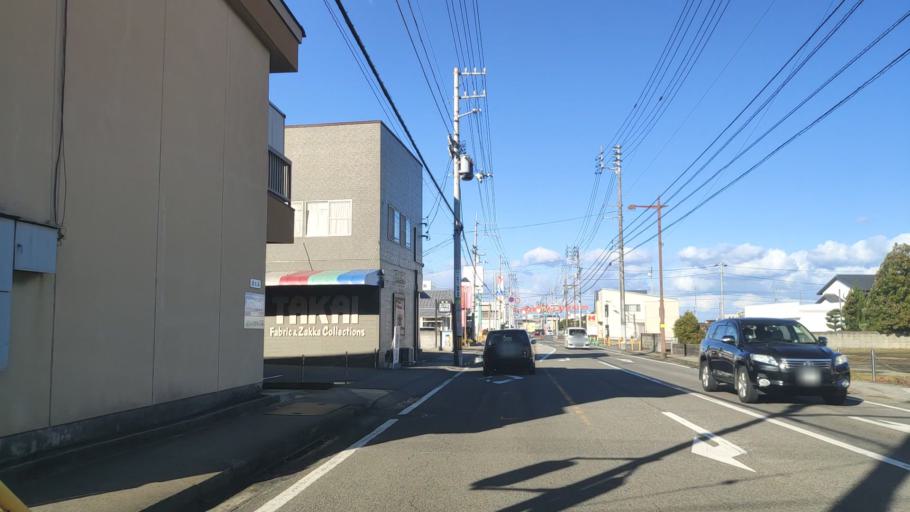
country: JP
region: Ehime
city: Saijo
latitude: 33.9185
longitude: 133.1919
